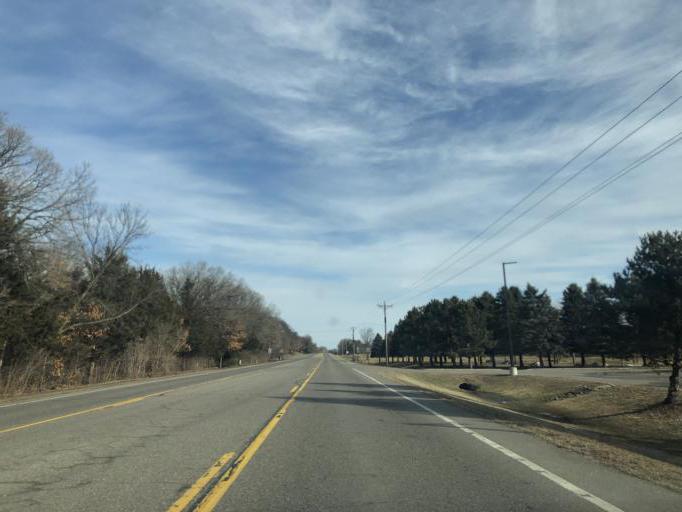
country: US
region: Minnesota
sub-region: Sherburne County
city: Becker
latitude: 45.4063
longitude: -93.8705
